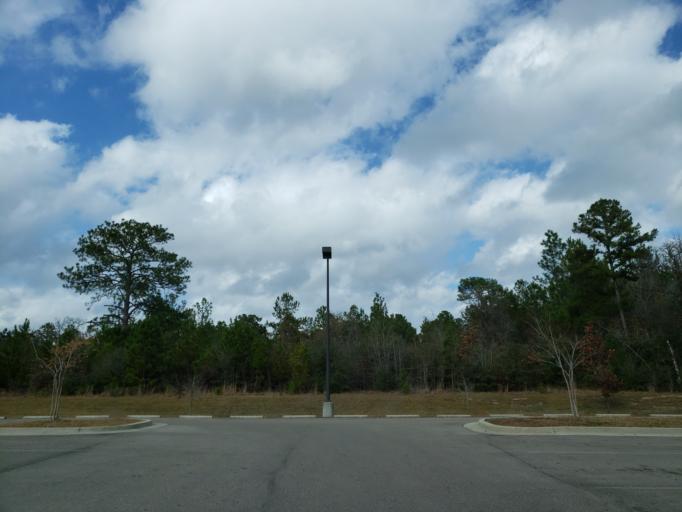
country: US
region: Mississippi
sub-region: Lamar County
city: West Hattiesburg
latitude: 31.3023
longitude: -89.3630
